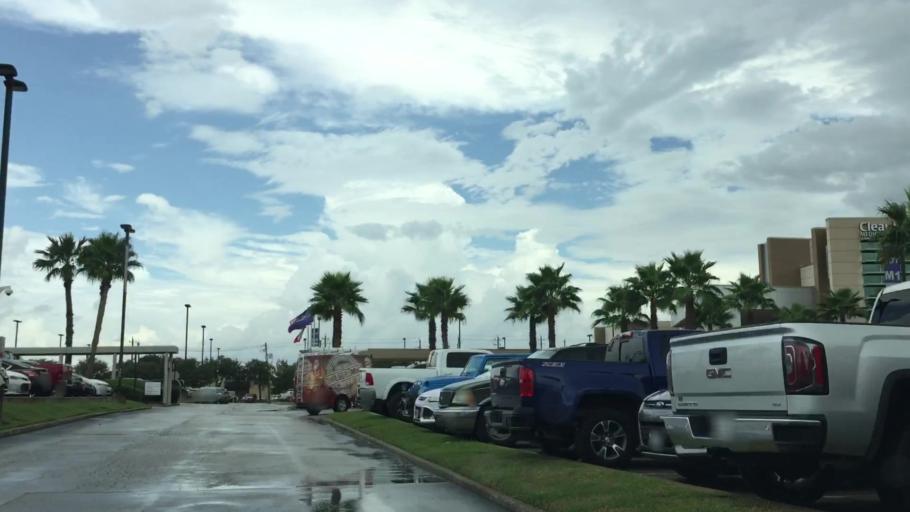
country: US
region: Texas
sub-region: Harris County
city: Webster
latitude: 29.5395
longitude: -95.1287
